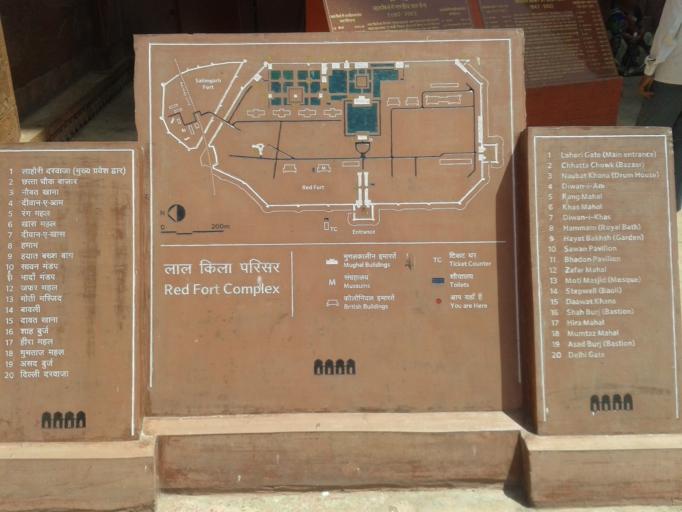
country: IN
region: NCT
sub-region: North Delhi
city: Delhi
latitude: 28.6561
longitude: 77.2385
